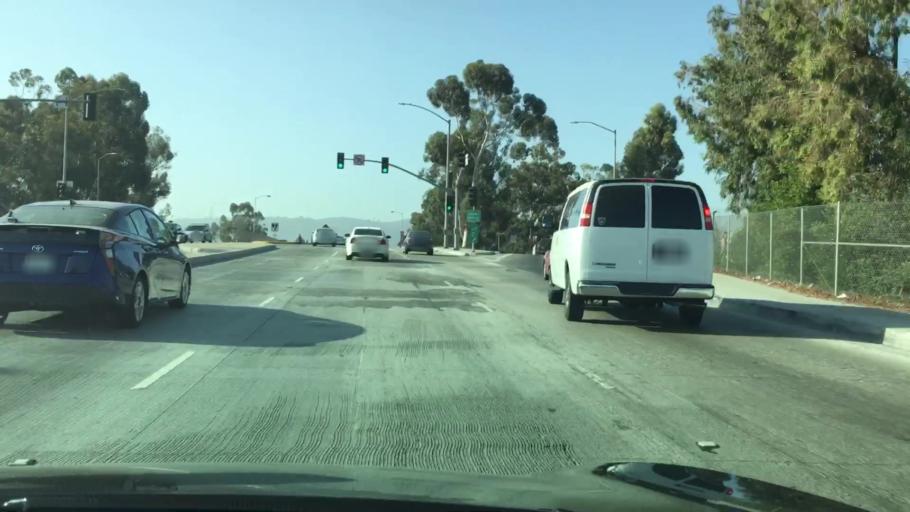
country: US
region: California
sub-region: Los Angeles County
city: South San Jose Hills
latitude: 33.9958
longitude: -117.8886
